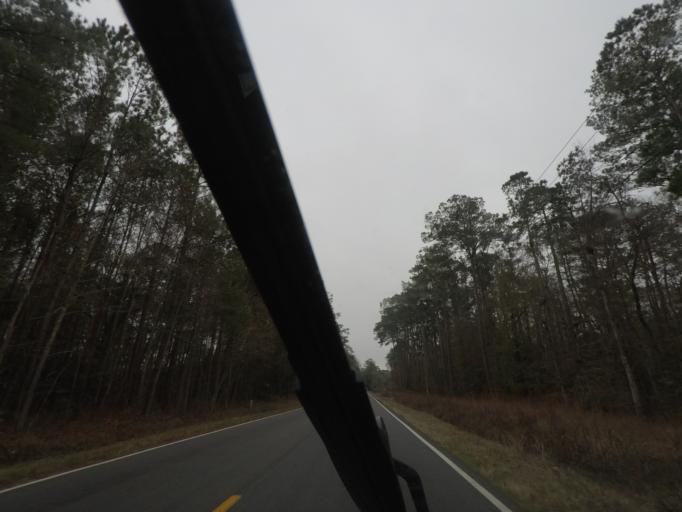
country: US
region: South Carolina
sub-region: Charleston County
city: Ravenel
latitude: 32.7425
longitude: -80.3493
